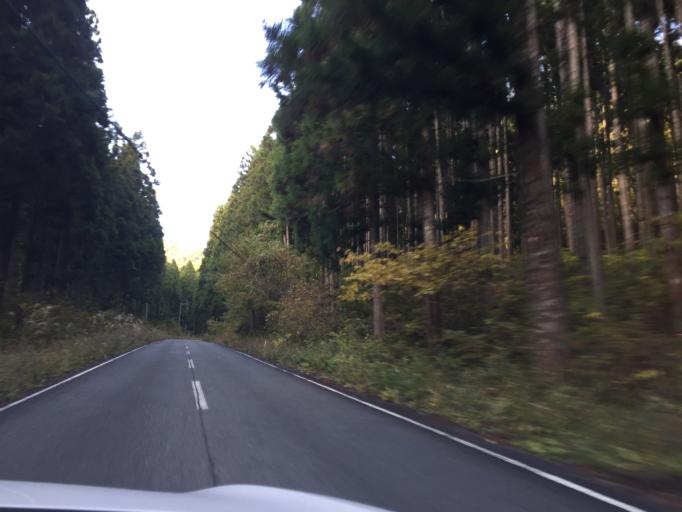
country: JP
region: Fukushima
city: Iwaki
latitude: 37.2380
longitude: 140.7632
